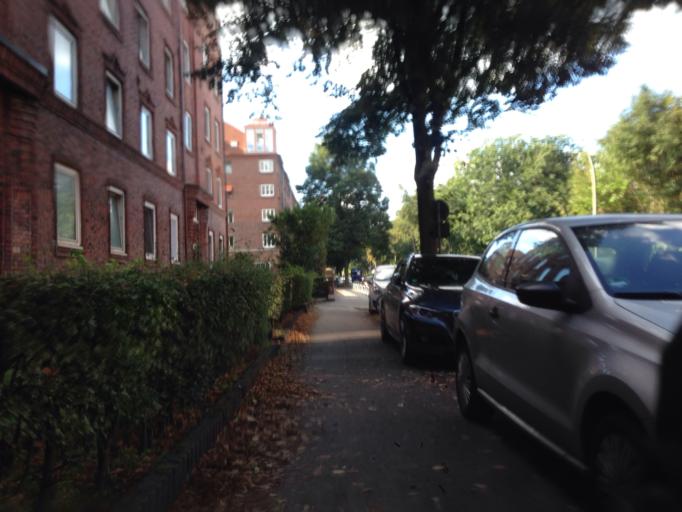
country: DE
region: Hamburg
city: Barmbek-Nord
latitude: 53.5831
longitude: 10.0549
